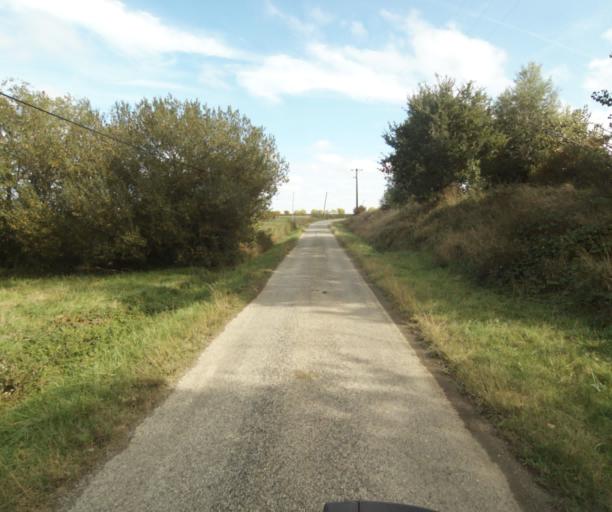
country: FR
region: Midi-Pyrenees
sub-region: Departement du Tarn-et-Garonne
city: Saint-Porquier
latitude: 43.9458
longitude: 1.1355
